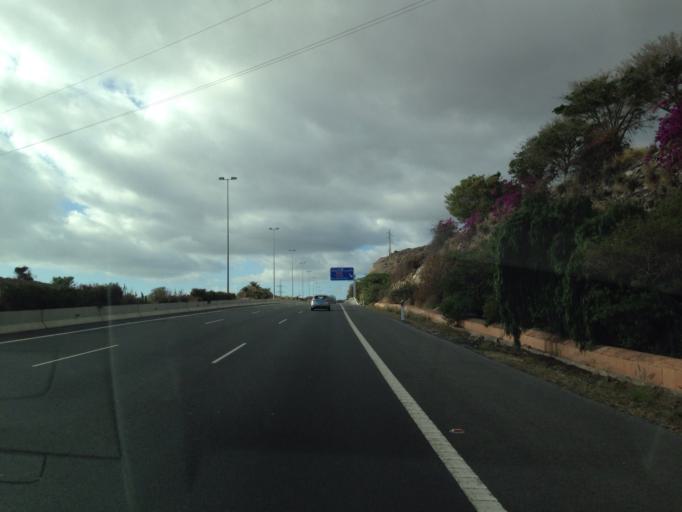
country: ES
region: Canary Islands
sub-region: Provincia de Las Palmas
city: Playa del Ingles
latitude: 27.7694
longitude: -15.5713
